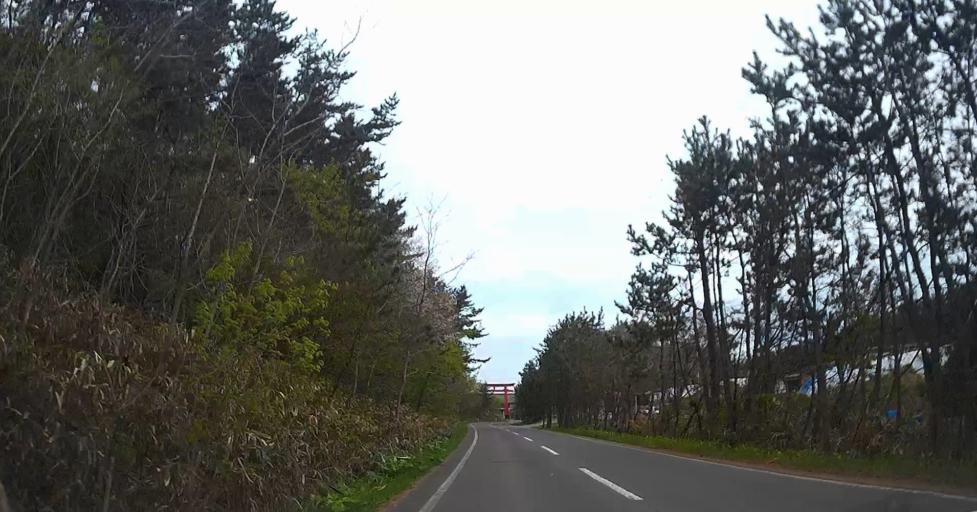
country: JP
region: Aomori
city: Shimokizukuri
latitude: 40.9382
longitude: 140.3158
